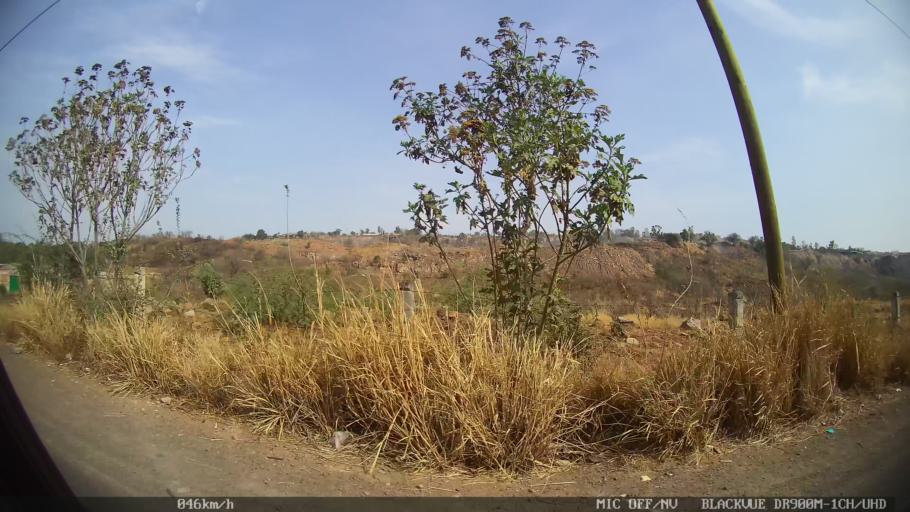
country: MX
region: Jalisco
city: Tonala
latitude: 20.6219
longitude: -103.2219
